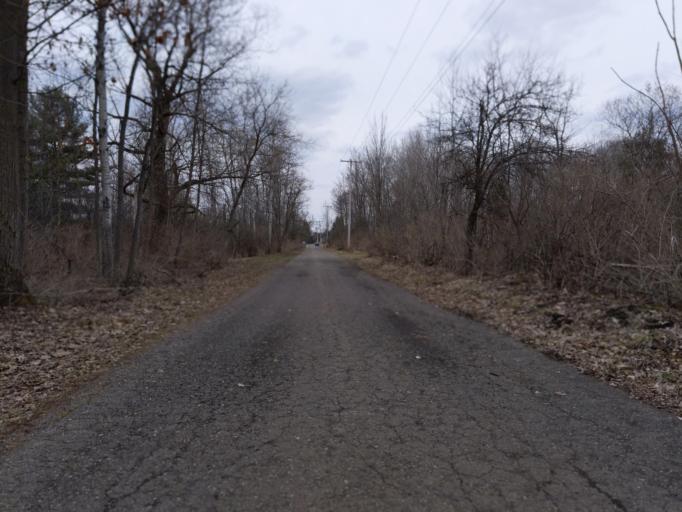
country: US
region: New York
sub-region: Tompkins County
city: Dryden
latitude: 42.5099
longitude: -76.3434
